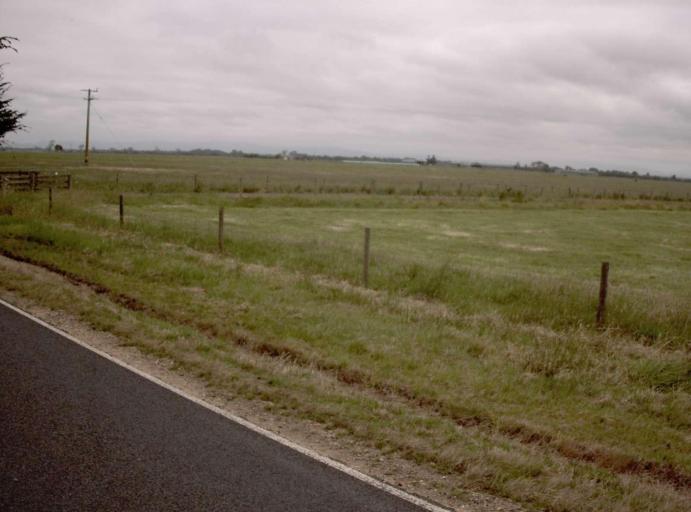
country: AU
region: Victoria
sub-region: Wellington
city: Sale
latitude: -38.0401
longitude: 146.9342
